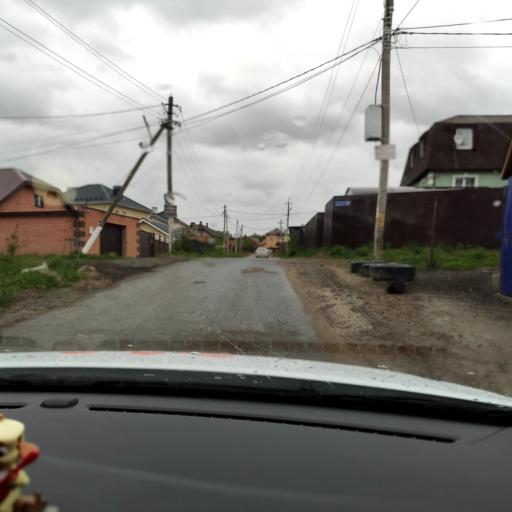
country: RU
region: Tatarstan
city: Stolbishchi
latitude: 55.7597
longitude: 49.2955
